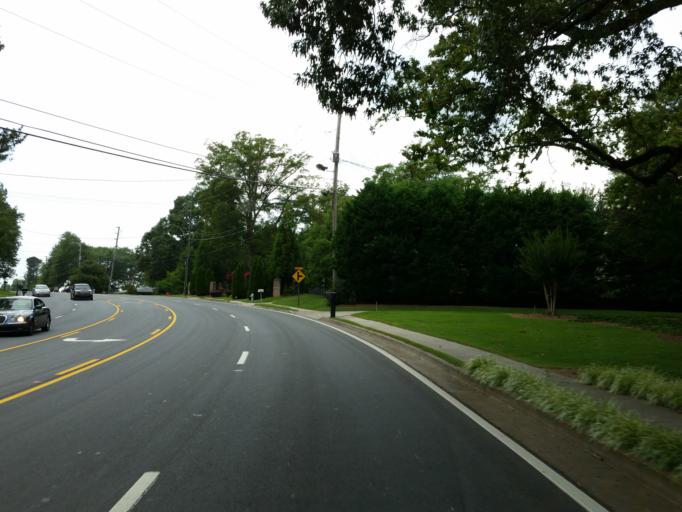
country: US
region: Georgia
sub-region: Cobb County
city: Marietta
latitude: 33.9831
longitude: -84.4786
